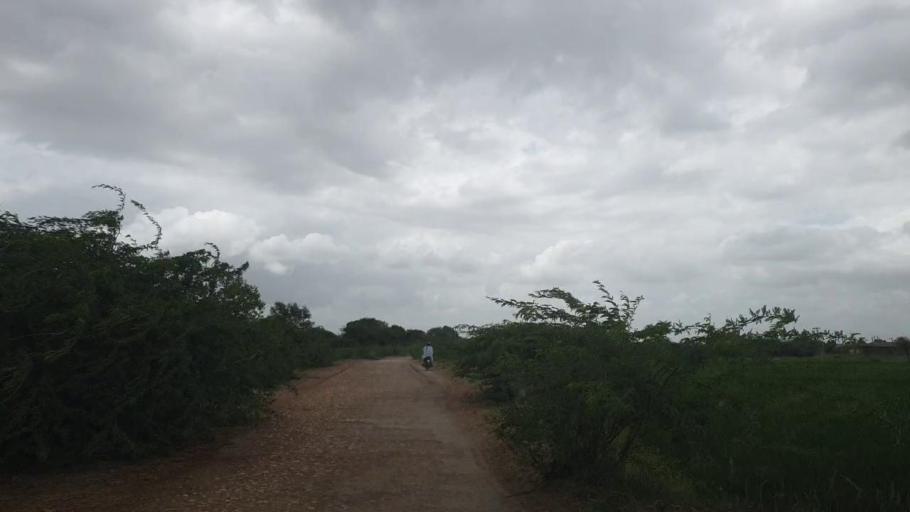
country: PK
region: Sindh
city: Badin
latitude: 24.6580
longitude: 68.9478
